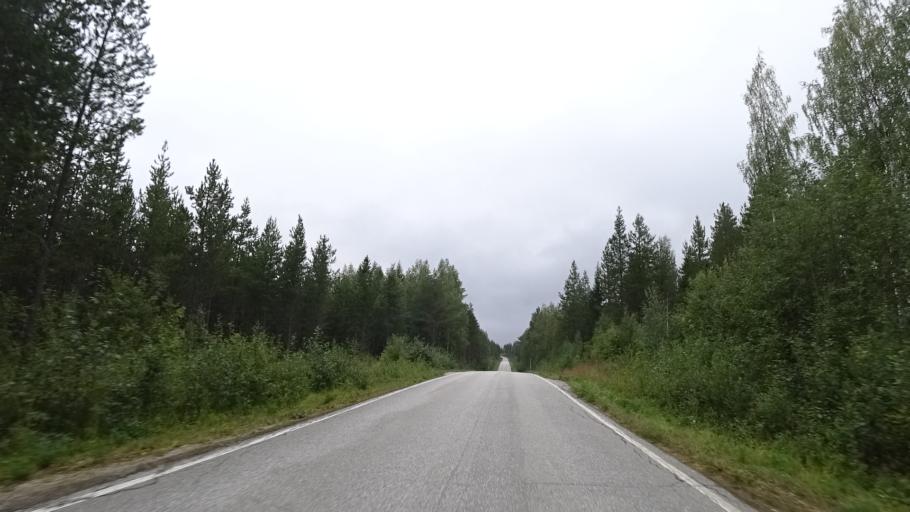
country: FI
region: North Karelia
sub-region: Pielisen Karjala
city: Lieksa
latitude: 63.3735
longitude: 30.3029
